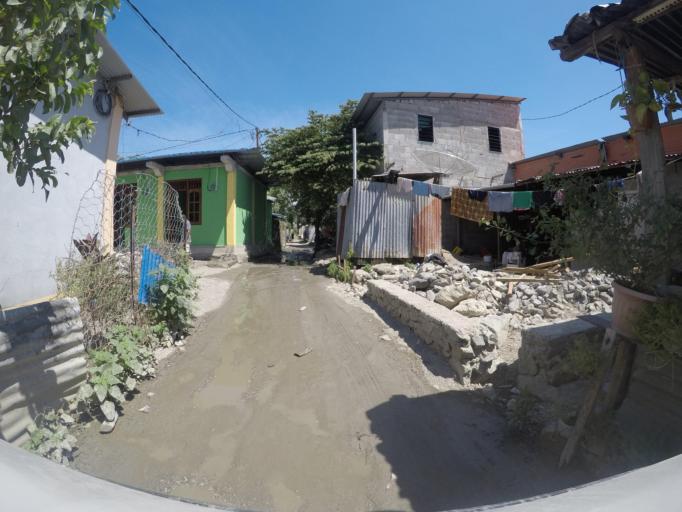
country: TL
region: Dili
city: Dili
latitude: -8.5519
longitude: 125.5372
